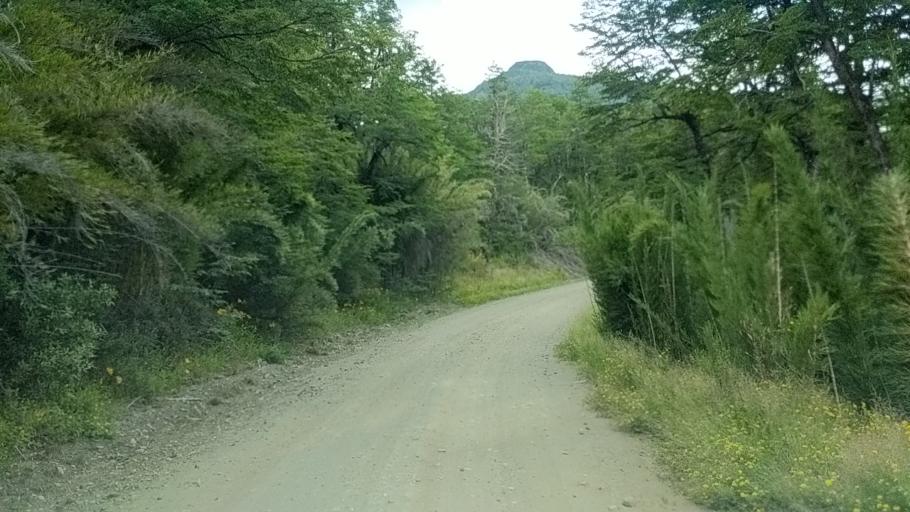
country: AR
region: Neuquen
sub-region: Departamento de Lacar
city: San Martin de los Andes
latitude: -39.8255
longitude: -71.6414
